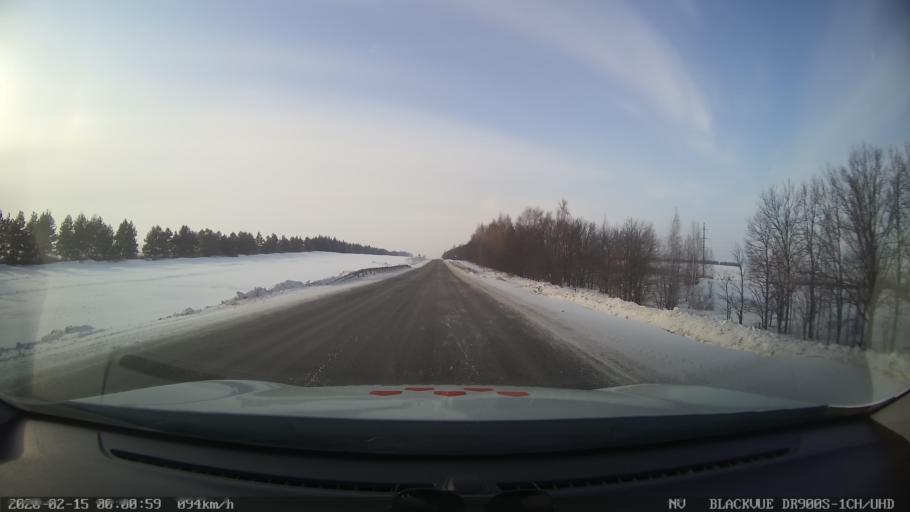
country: RU
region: Tatarstan
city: Kuybyshevskiy Zaton
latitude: 55.3450
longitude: 49.0259
